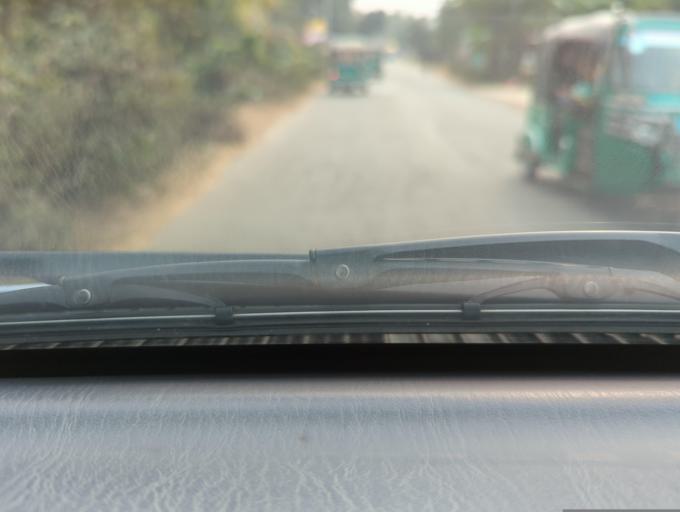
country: BD
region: Sylhet
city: Maulavi Bazar
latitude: 24.4947
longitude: 91.7470
